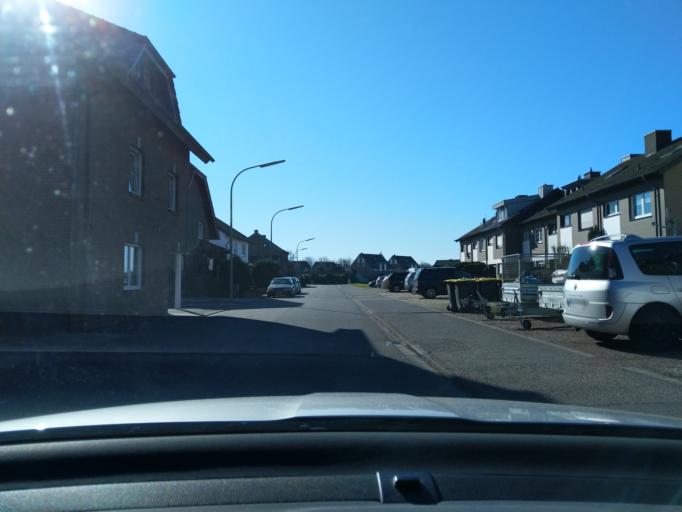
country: DE
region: North Rhine-Westphalia
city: Wegberg
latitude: 51.1405
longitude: 6.2951
